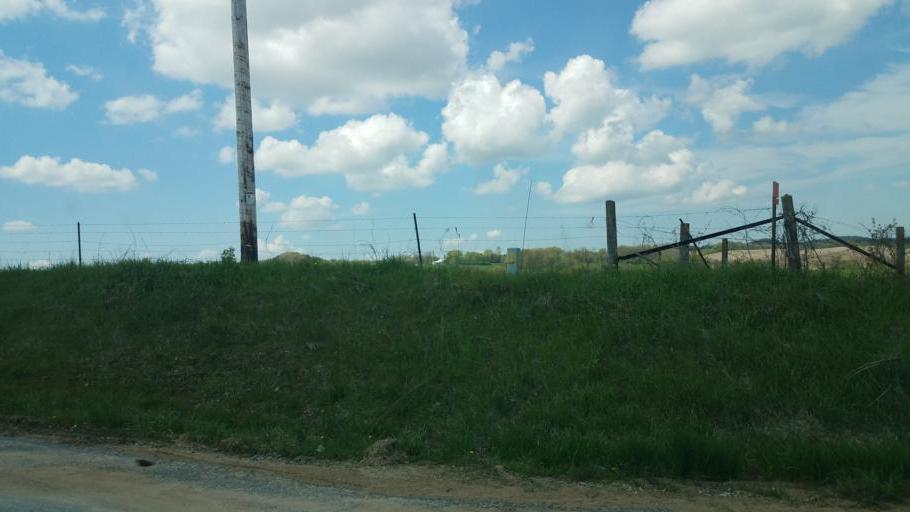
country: US
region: Wisconsin
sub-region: Vernon County
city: Hillsboro
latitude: 43.6848
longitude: -90.3323
